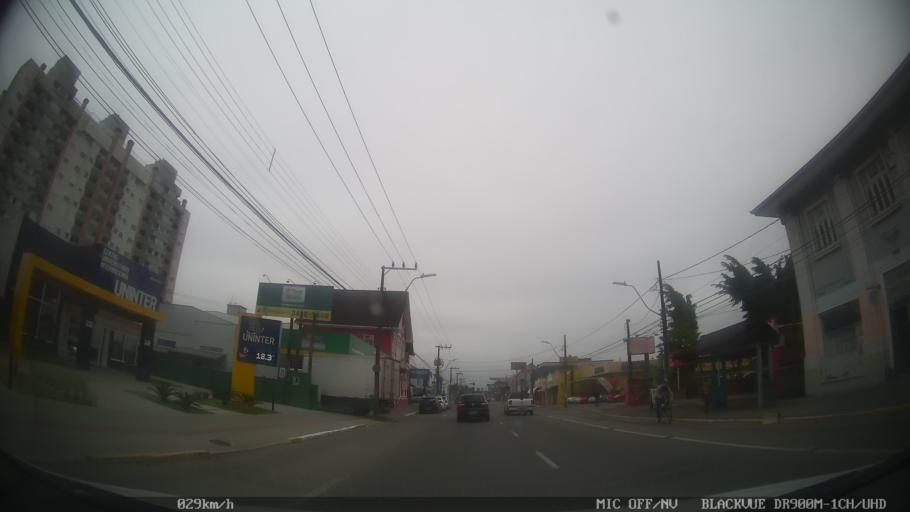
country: BR
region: Santa Catarina
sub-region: Joinville
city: Joinville
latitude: -26.3152
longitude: -48.8453
